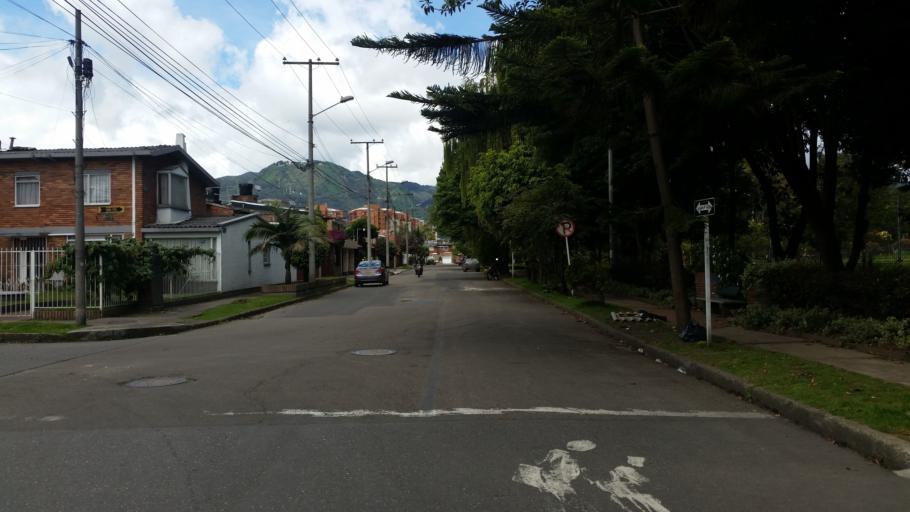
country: CO
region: Bogota D.C.
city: Bogota
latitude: 4.6472
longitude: -74.0898
